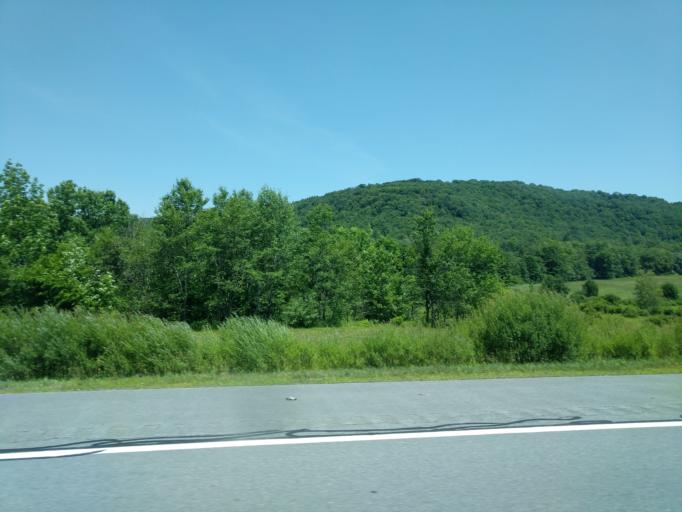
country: US
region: New York
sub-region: Sullivan County
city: Livingston Manor
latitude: 41.9161
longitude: -74.8392
